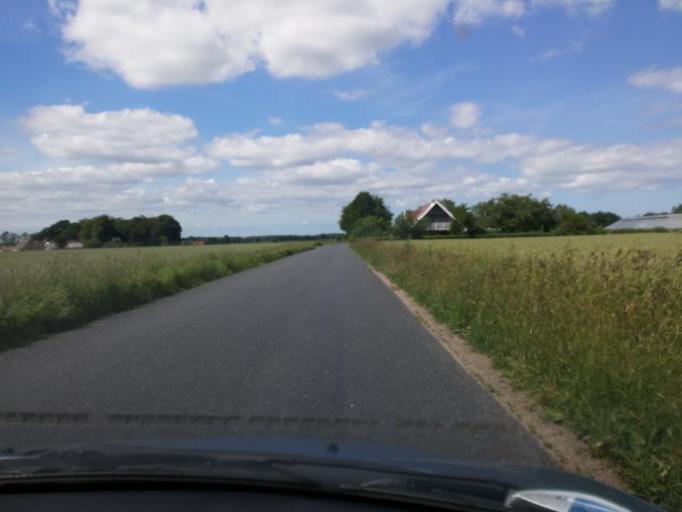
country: DK
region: South Denmark
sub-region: Kerteminde Kommune
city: Langeskov
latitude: 55.4106
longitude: 10.5799
